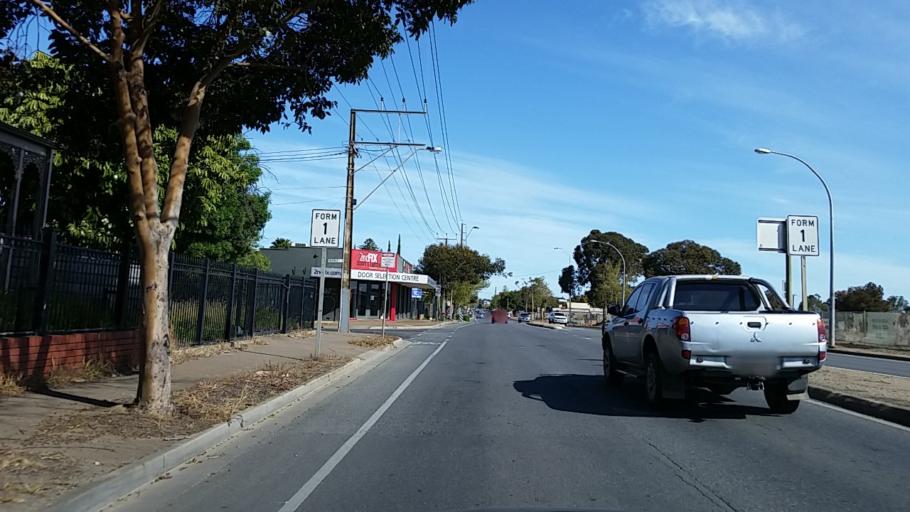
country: AU
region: South Australia
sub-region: Prospect
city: Prospect
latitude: -34.8760
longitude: 138.5843
